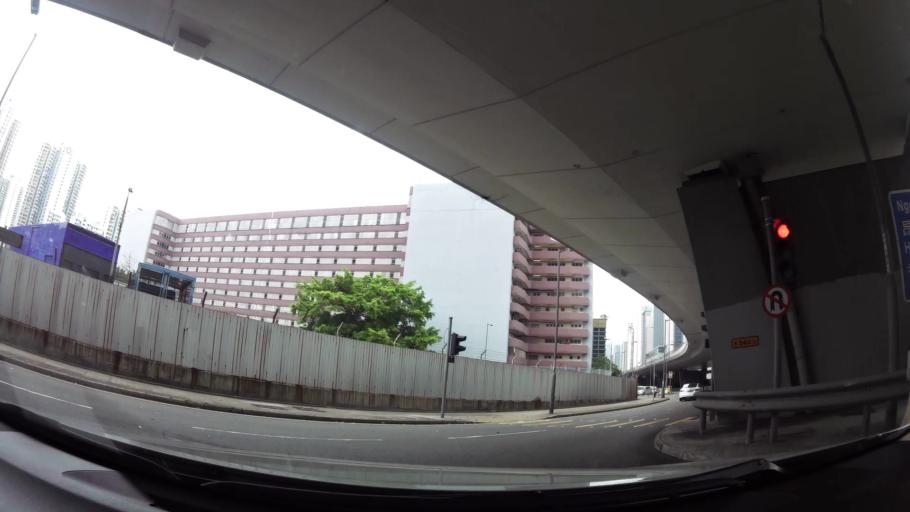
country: HK
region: Sham Shui Po
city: Sham Shui Po
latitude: 22.3340
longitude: 114.1506
